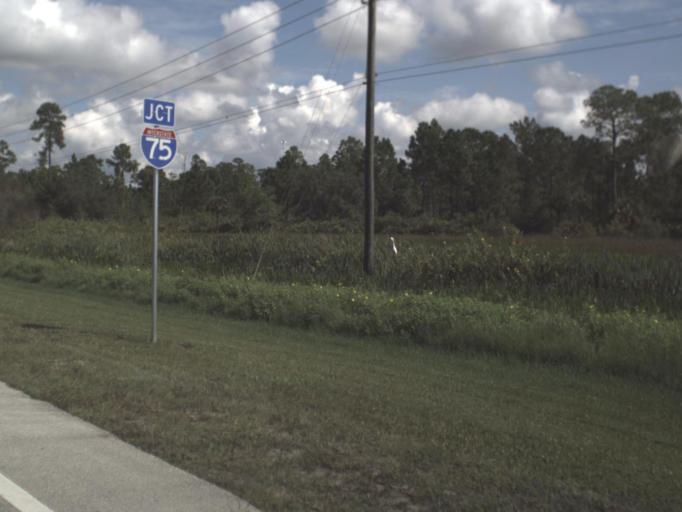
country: US
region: Florida
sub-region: Sarasota County
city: North Port
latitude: 27.0946
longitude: -82.1554
